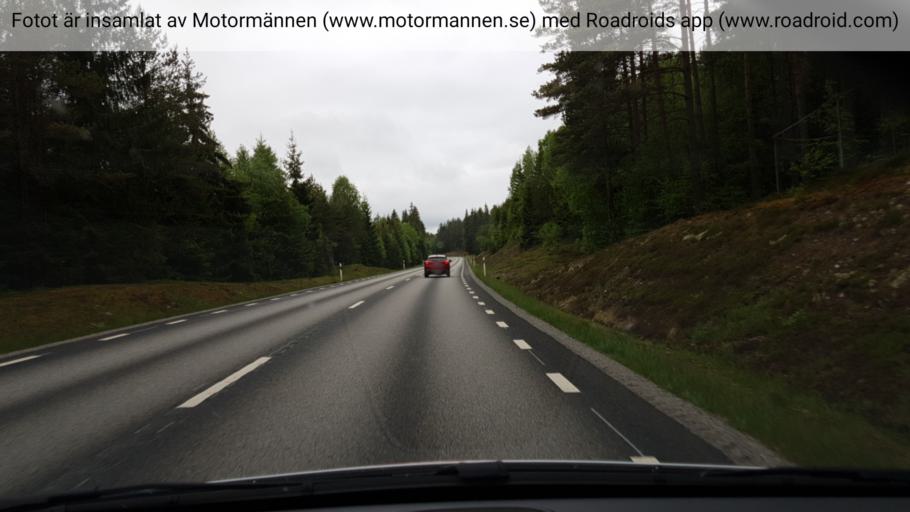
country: SE
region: Joenkoeping
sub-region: Gnosjo Kommun
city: Gnosjoe
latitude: 57.5180
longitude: 13.6817
